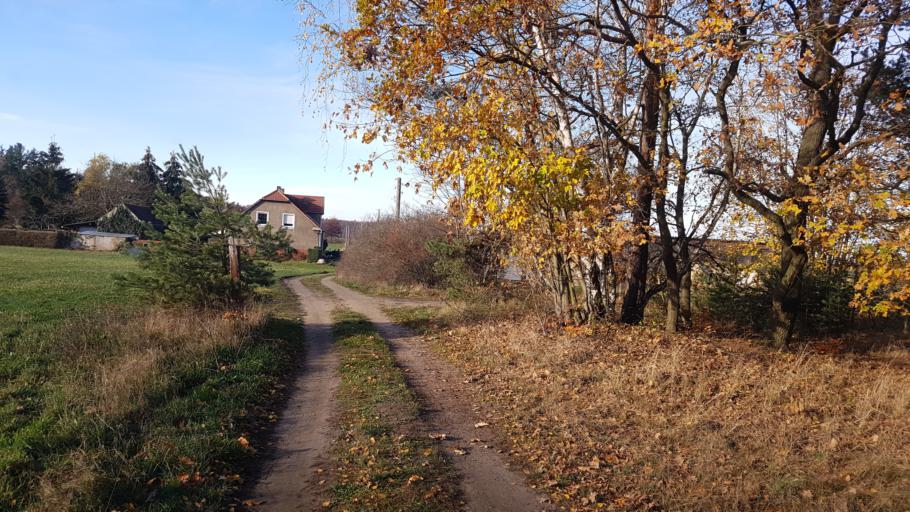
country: DE
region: Brandenburg
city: Sallgast
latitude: 51.5835
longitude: 13.8603
